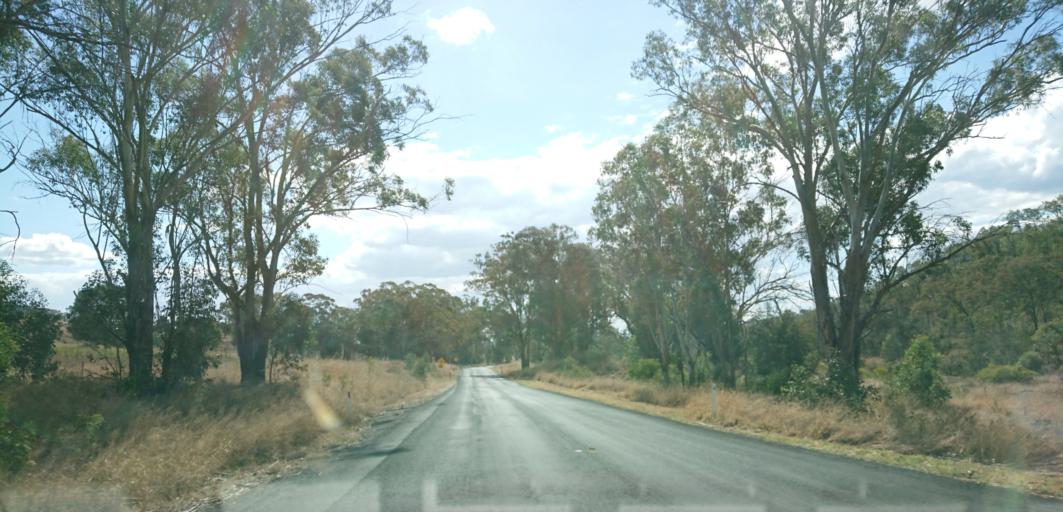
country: AU
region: Queensland
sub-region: Toowoomba
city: Top Camp
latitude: -27.8019
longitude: 152.1060
